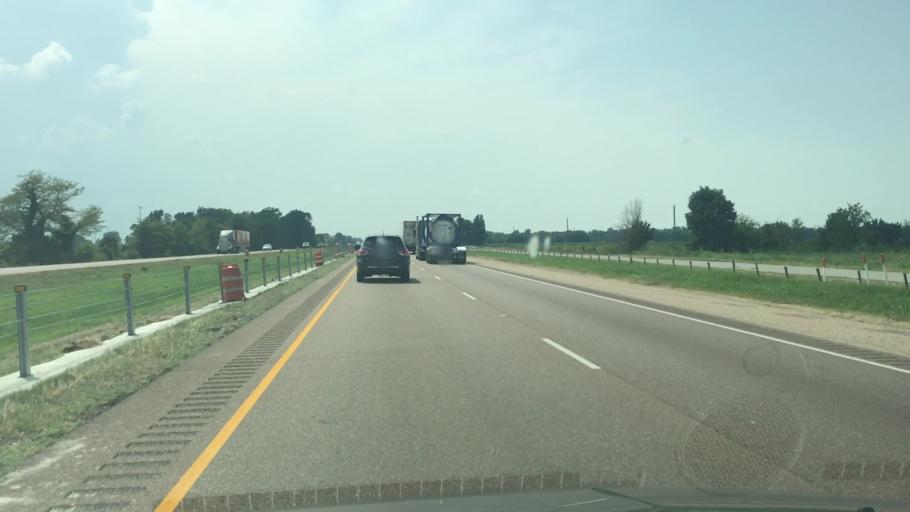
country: US
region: Arkansas
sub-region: Crittenden County
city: West Memphis
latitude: 35.1489
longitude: -90.3400
